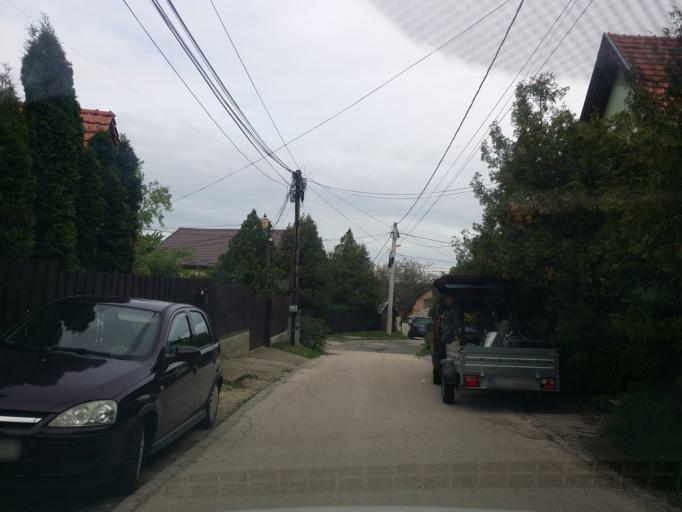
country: HU
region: Pest
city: Biatorbagy
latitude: 47.4766
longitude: 18.8314
